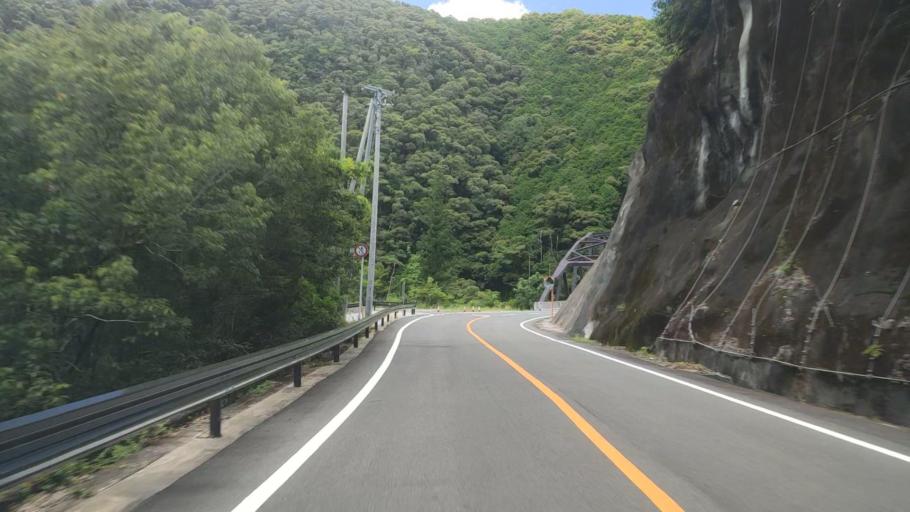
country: JP
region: Mie
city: Owase
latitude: 34.0018
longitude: 136.0093
